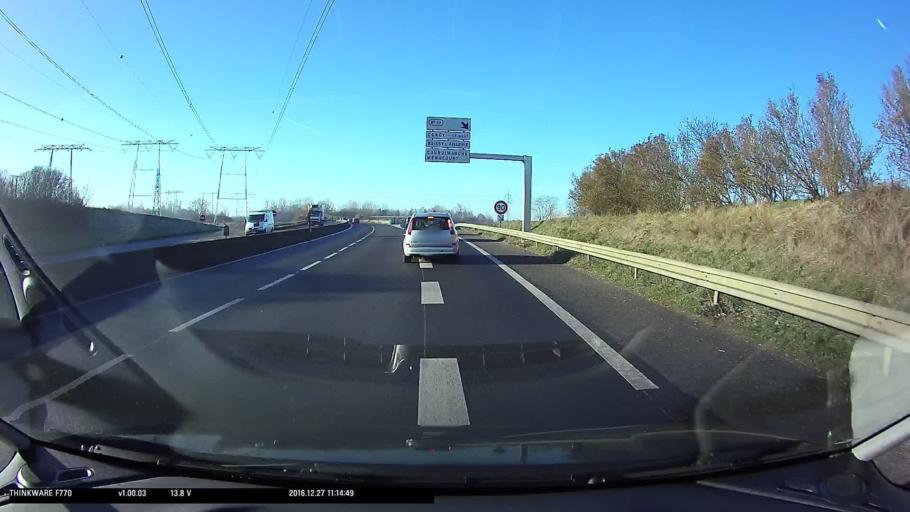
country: FR
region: Ile-de-France
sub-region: Departement du Val-d'Oise
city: Courdimanche
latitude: 49.0602
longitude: 2.0143
